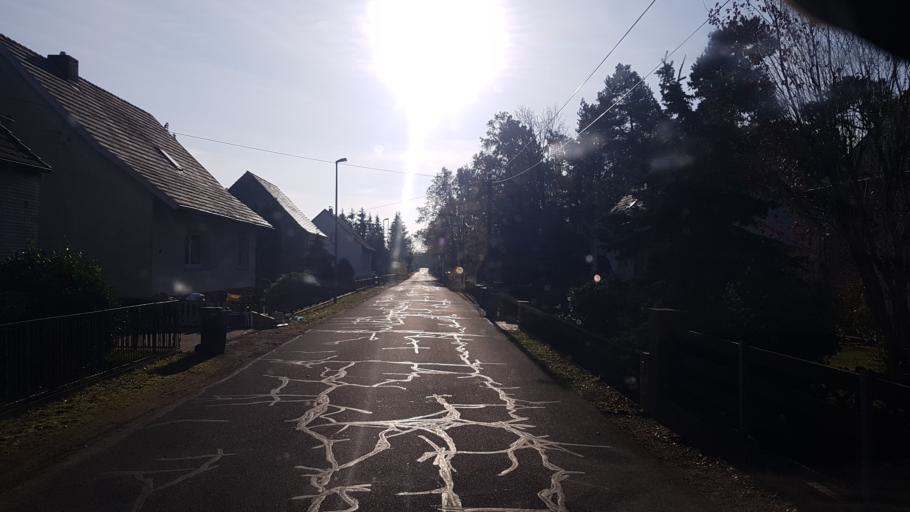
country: DE
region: Brandenburg
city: Schipkau
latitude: 51.5549
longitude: 13.9283
